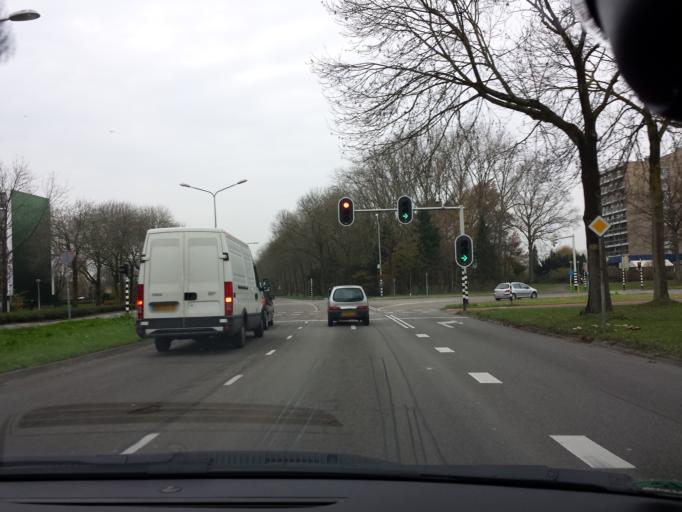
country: NL
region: Gelderland
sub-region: Gemeente Nijmegen
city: Lindenholt
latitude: 51.8043
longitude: 5.8071
